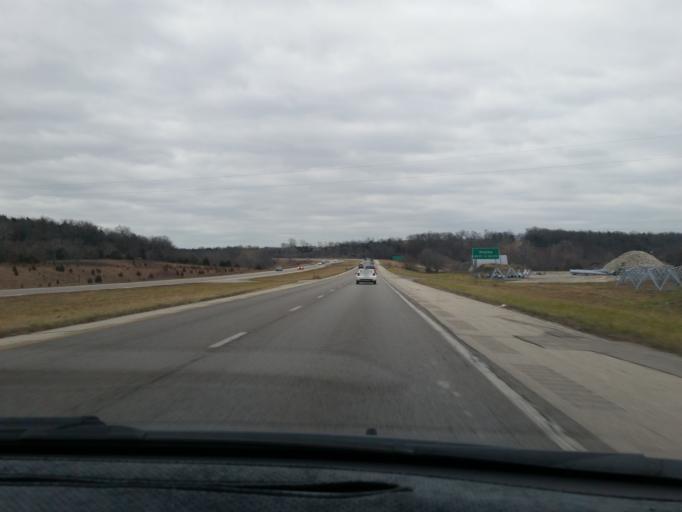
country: US
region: Kansas
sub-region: Johnson County
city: De Soto
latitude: 38.9527
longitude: -94.9087
